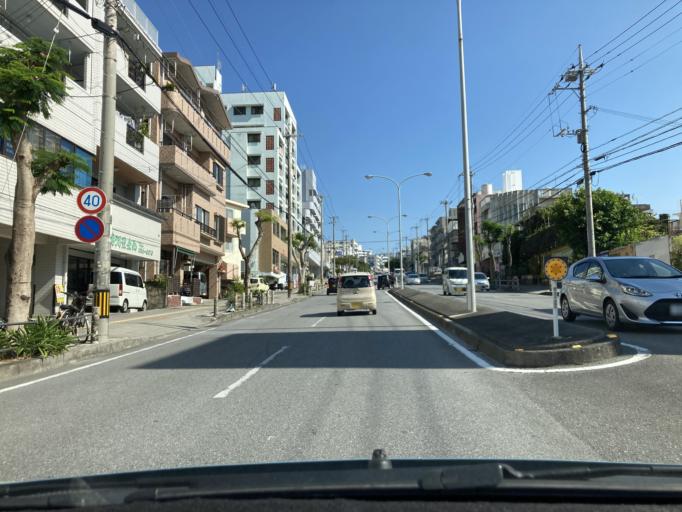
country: JP
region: Okinawa
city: Naha-shi
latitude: 26.2059
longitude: 127.7015
